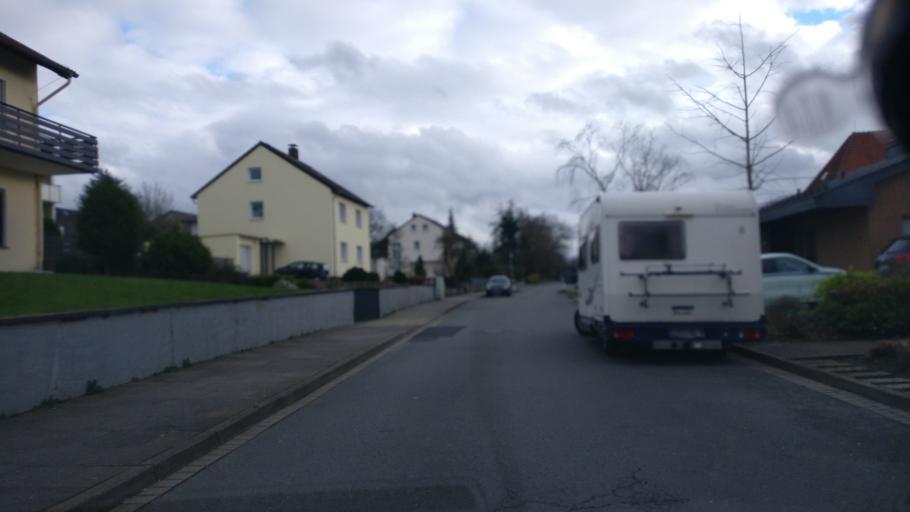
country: DE
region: North Rhine-Westphalia
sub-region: Regierungsbezirk Detmold
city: Lage
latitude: 52.0137
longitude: 8.7721
